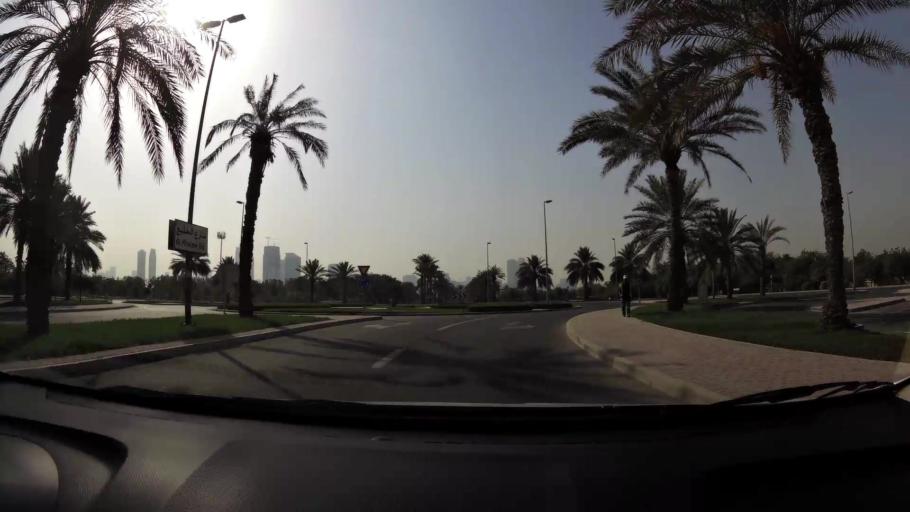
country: AE
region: Ash Shariqah
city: Sharjah
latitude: 25.3170
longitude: 55.3462
